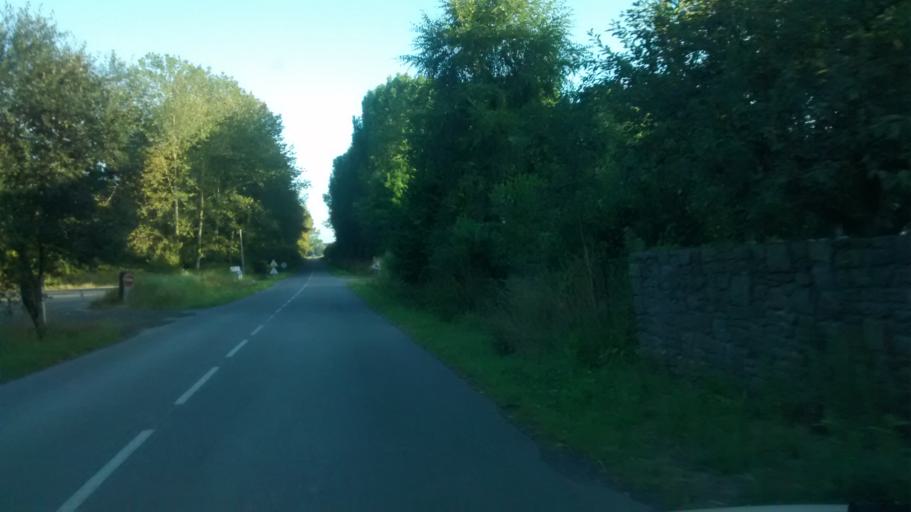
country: FR
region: Brittany
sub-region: Departement d'Ille-et-Vilaine
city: Plerguer
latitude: 48.5463
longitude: -1.8635
